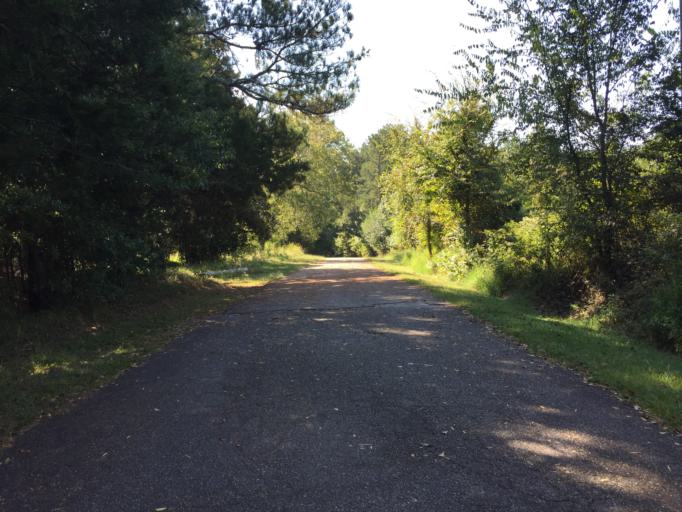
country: US
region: Georgia
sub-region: Gwinnett County
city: Duluth
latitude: 34.0414
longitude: -84.1411
